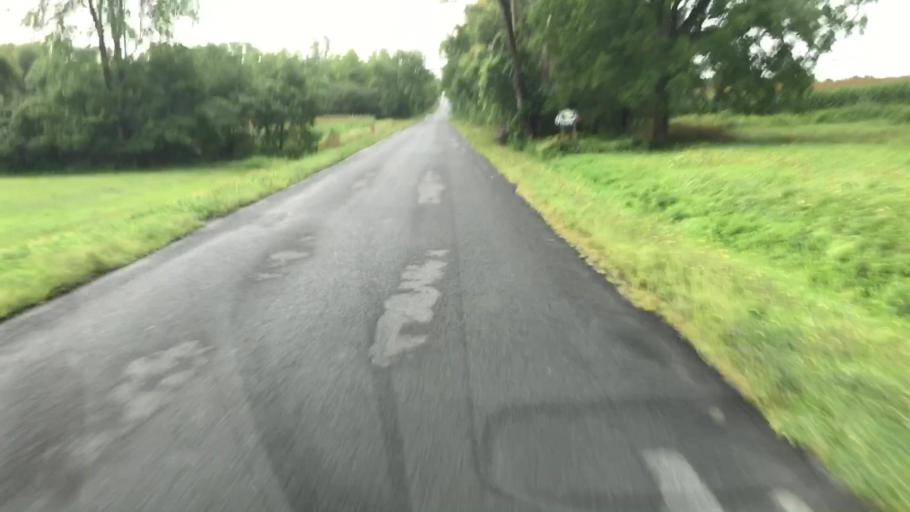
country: US
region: New York
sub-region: Cayuga County
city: Melrose Park
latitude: 42.9273
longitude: -76.5084
